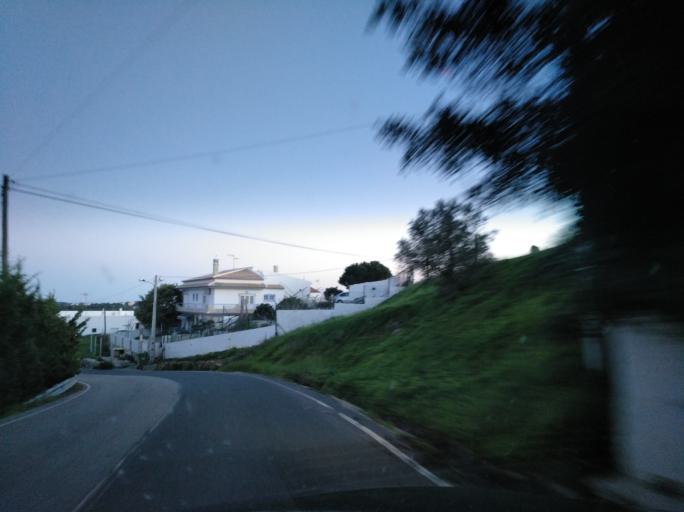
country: PT
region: Faro
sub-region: Vila Real de Santo Antonio
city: Monte Gordo
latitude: 37.2034
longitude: -7.5133
